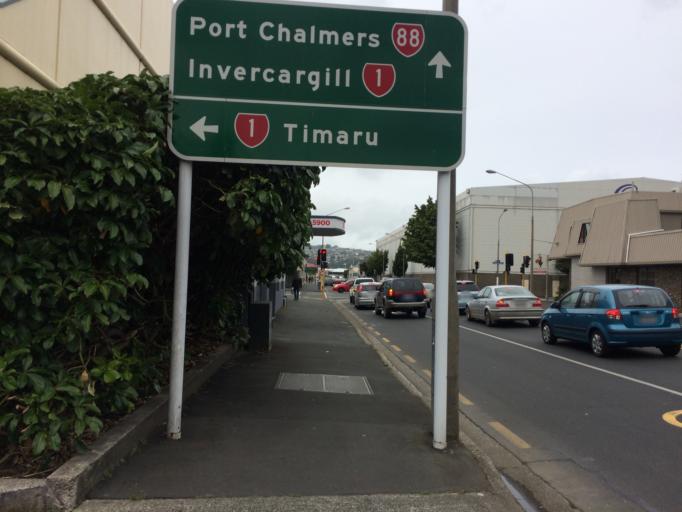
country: NZ
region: Otago
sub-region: Dunedin City
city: Dunedin
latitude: -45.8722
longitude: 170.5072
